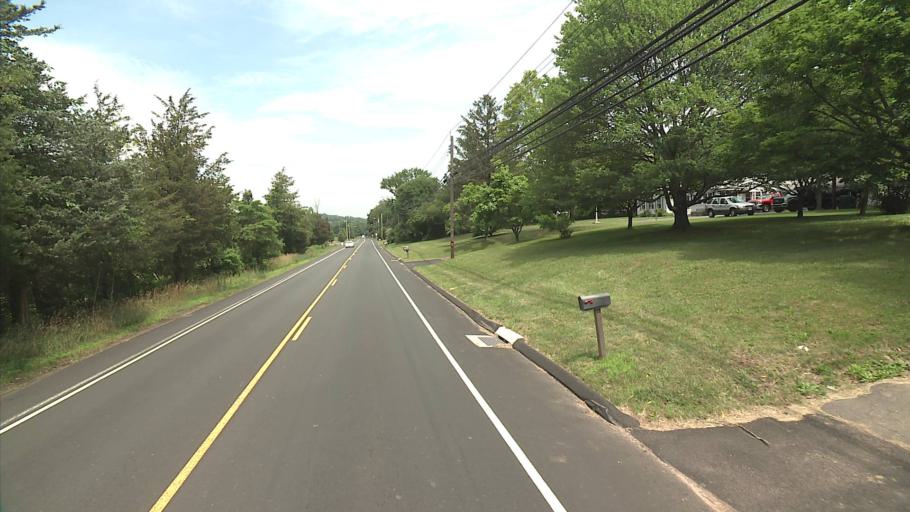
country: US
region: Connecticut
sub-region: New Haven County
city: North Branford
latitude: 41.3501
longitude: -72.8016
